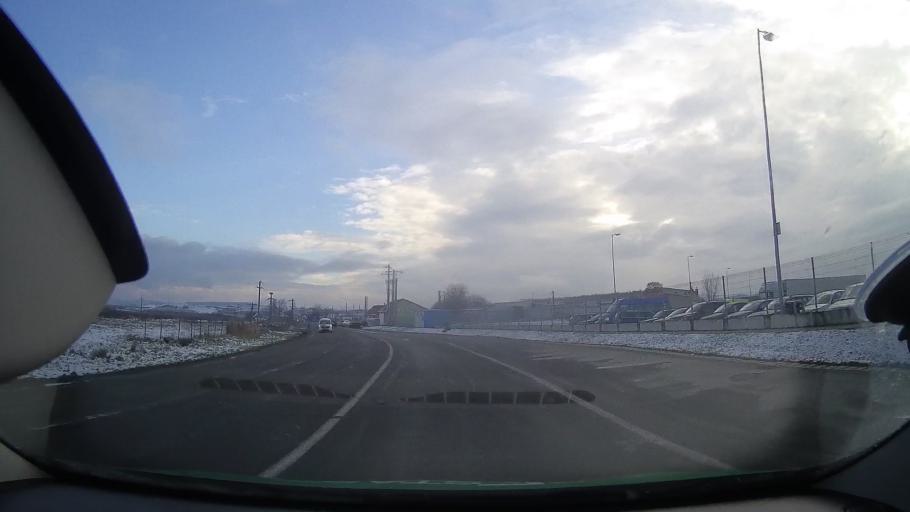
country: RO
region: Mures
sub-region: Comuna Iernut
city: Iernut
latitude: 46.4347
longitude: 24.2531
